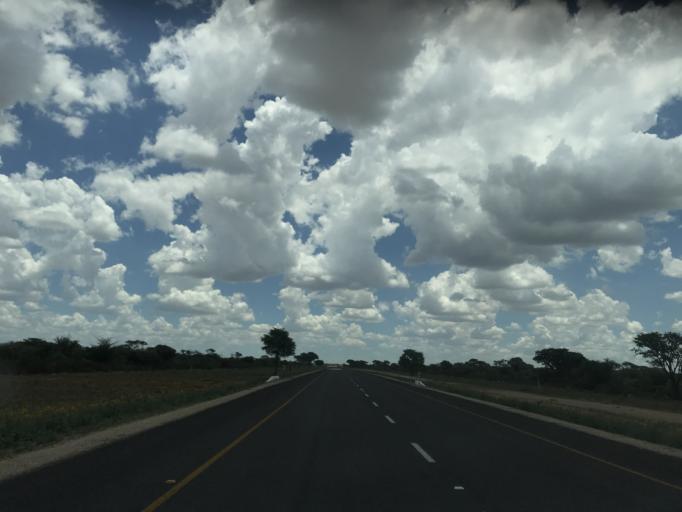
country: BW
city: Mabuli
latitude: -25.8027
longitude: 24.8409
